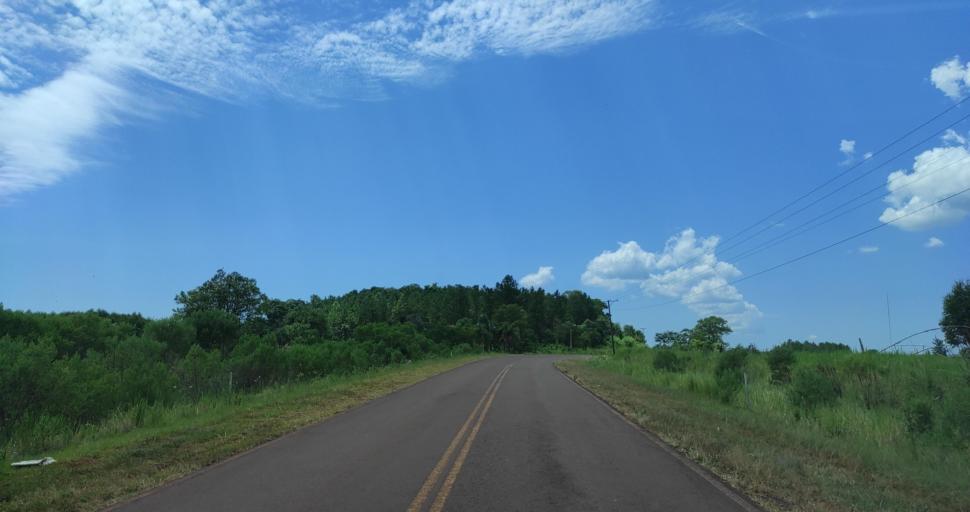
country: AR
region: Misiones
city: Ruiz de Montoya
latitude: -27.0192
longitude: -55.0352
